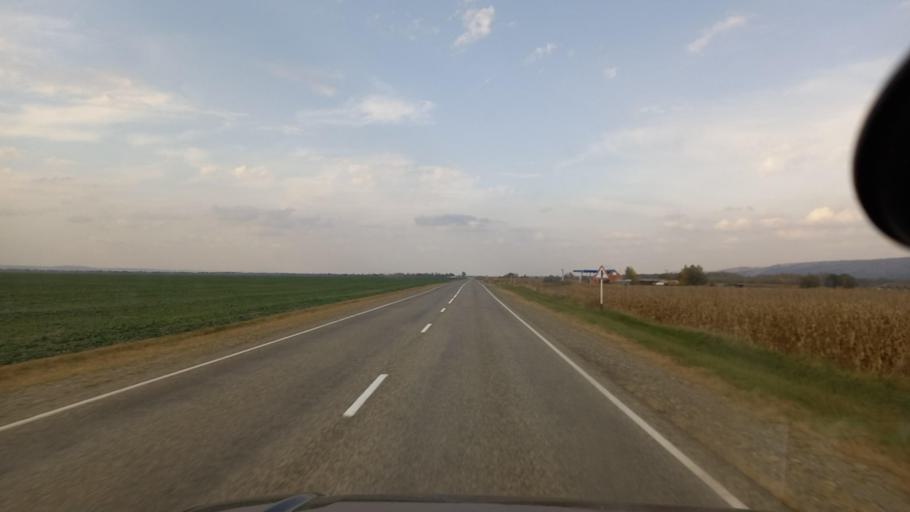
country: RU
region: Krasnodarskiy
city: Perepravnaya
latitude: 44.3304
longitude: 40.8486
